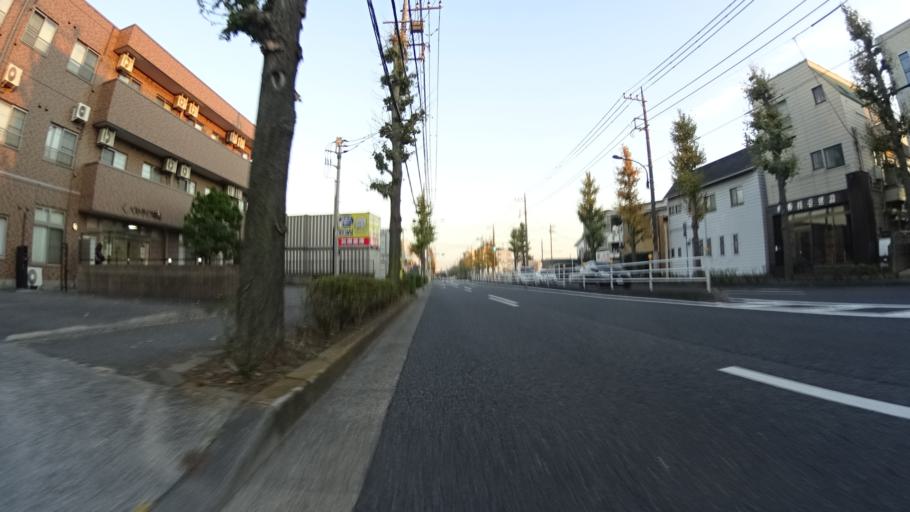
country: JP
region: Tokyo
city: Fussa
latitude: 35.7040
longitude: 139.3540
